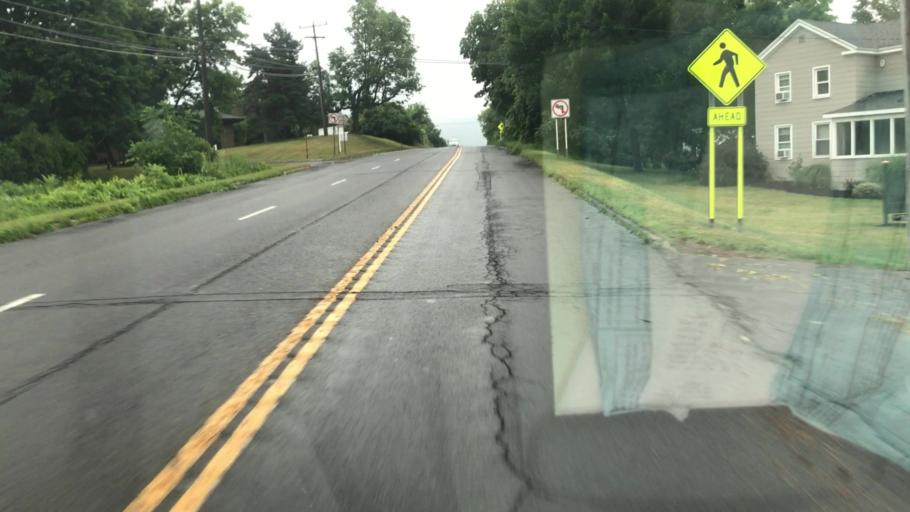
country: US
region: New York
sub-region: Onondaga County
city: Fayetteville
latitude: 43.0272
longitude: -76.0429
